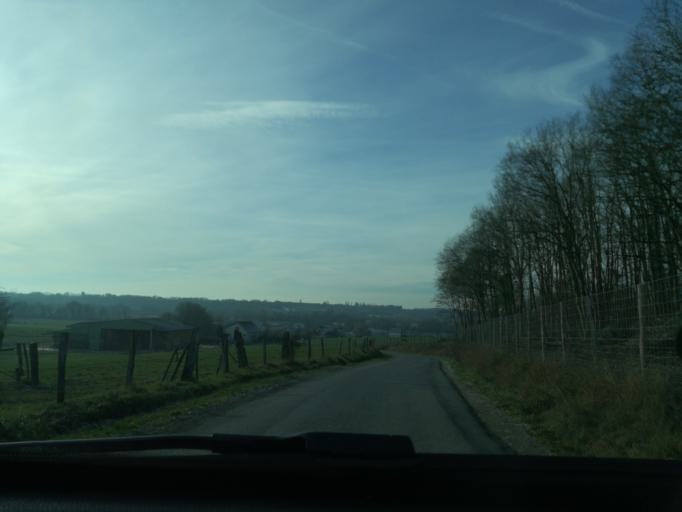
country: FR
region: Lorraine
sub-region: Departement de la Meuse
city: Revigny-sur-Ornain
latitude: 48.8270
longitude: 5.0576
